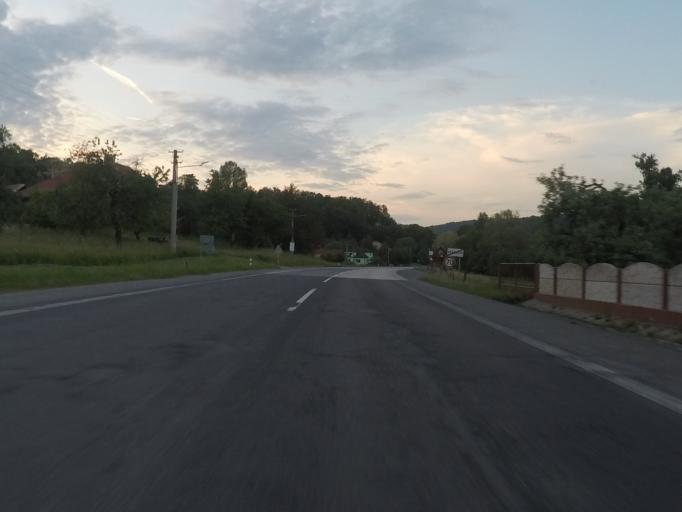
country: SK
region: Banskobystricky
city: Rimavska Sobota
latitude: 48.4713
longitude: 19.9498
